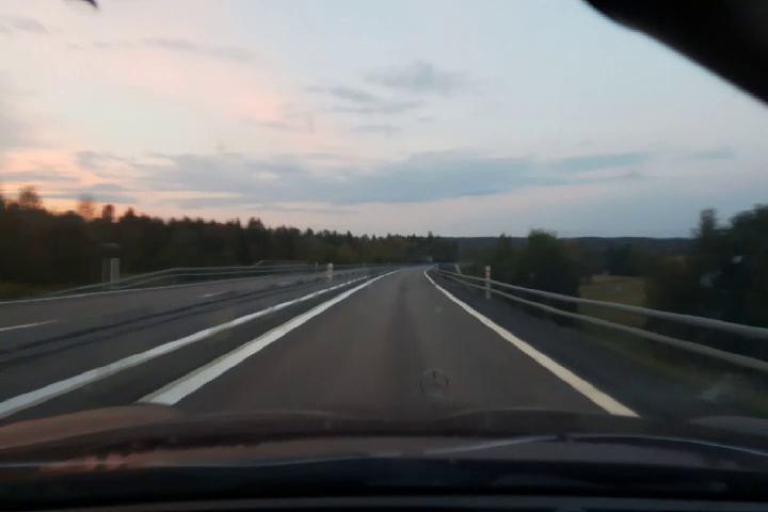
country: SE
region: Vaesternorrland
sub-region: Haernoesands Kommun
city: Haernoesand
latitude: 62.8722
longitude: 18.0456
